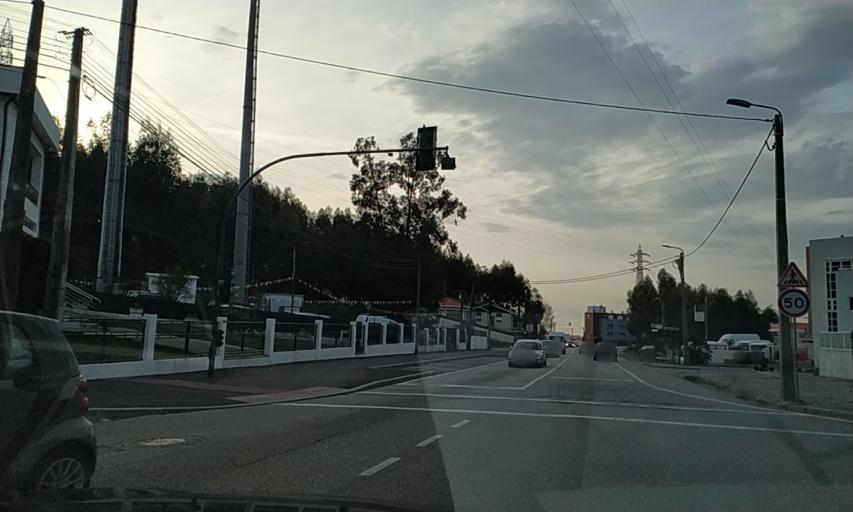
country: PT
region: Porto
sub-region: Gondomar
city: Baguim do Monte
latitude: 41.2055
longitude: -8.5290
